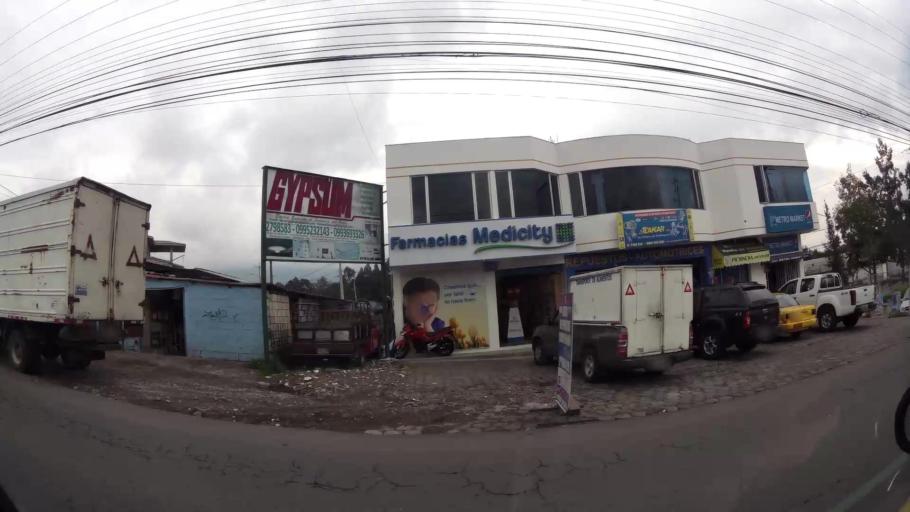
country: EC
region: Pichincha
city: Sangolqui
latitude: -0.3028
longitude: -78.4651
